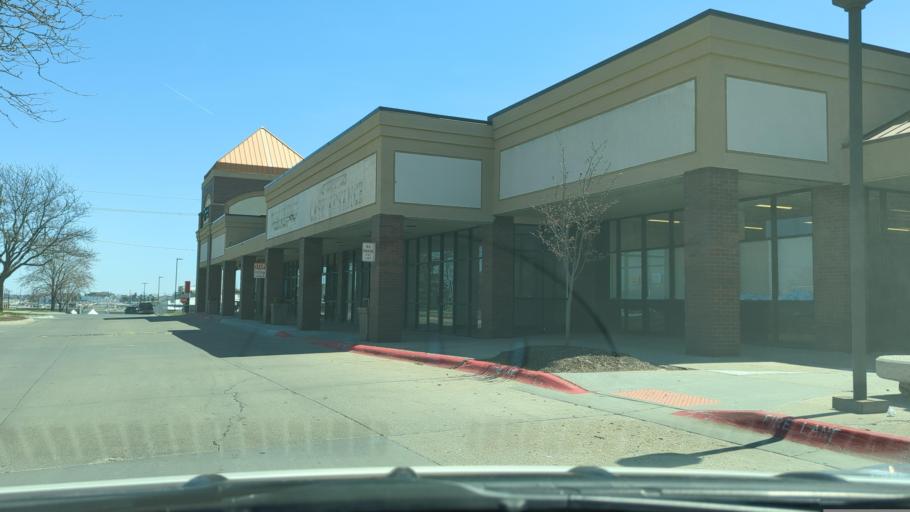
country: US
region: Nebraska
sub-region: Douglas County
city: Omaha
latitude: 41.2113
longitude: -95.9637
